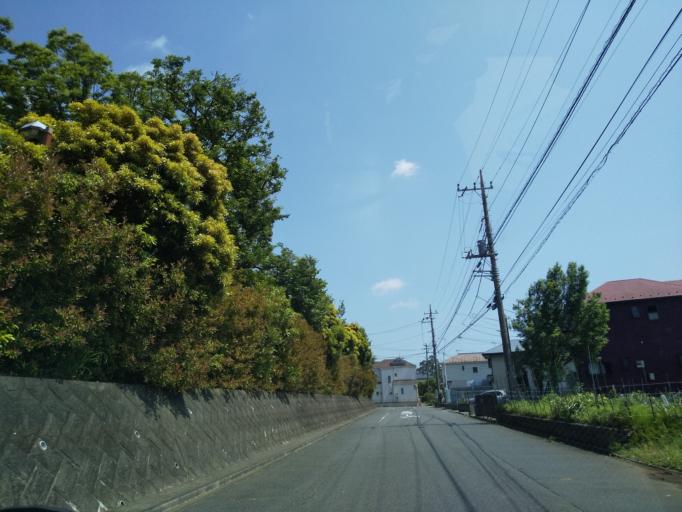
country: JP
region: Kanagawa
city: Zama
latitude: 35.4996
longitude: 139.3892
